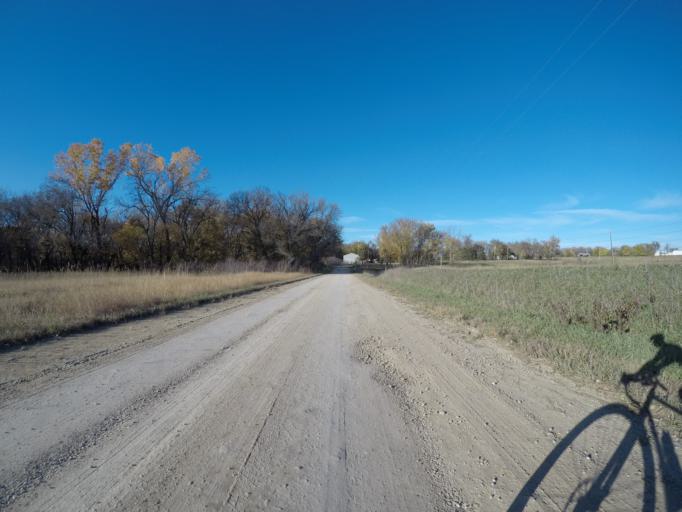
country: US
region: Kansas
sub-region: Riley County
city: Fort Riley North
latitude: 39.2754
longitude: -96.7844
